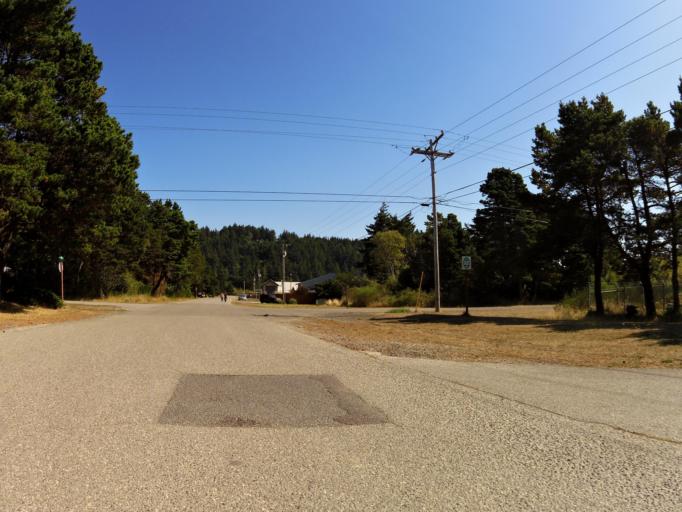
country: US
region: Oregon
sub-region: Curry County
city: Port Orford
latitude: 42.7496
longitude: -124.5009
